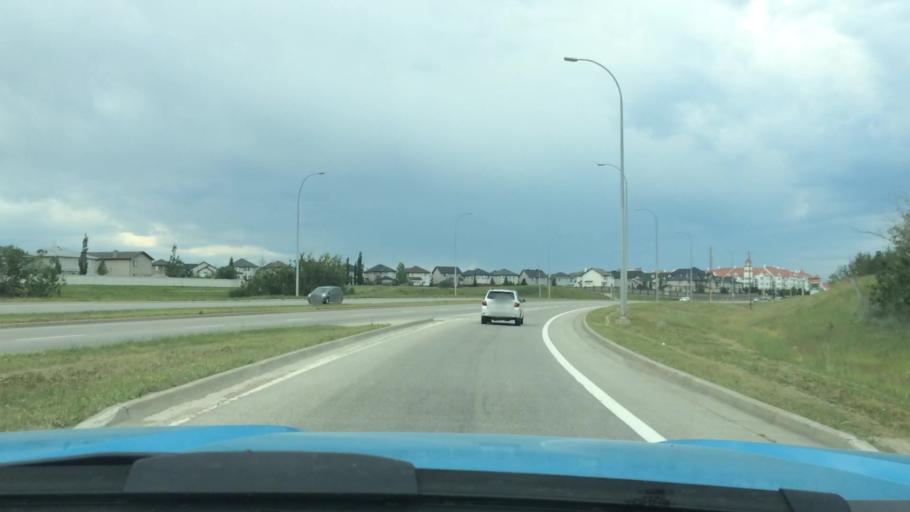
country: CA
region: Alberta
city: Calgary
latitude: 51.1467
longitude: -114.2085
